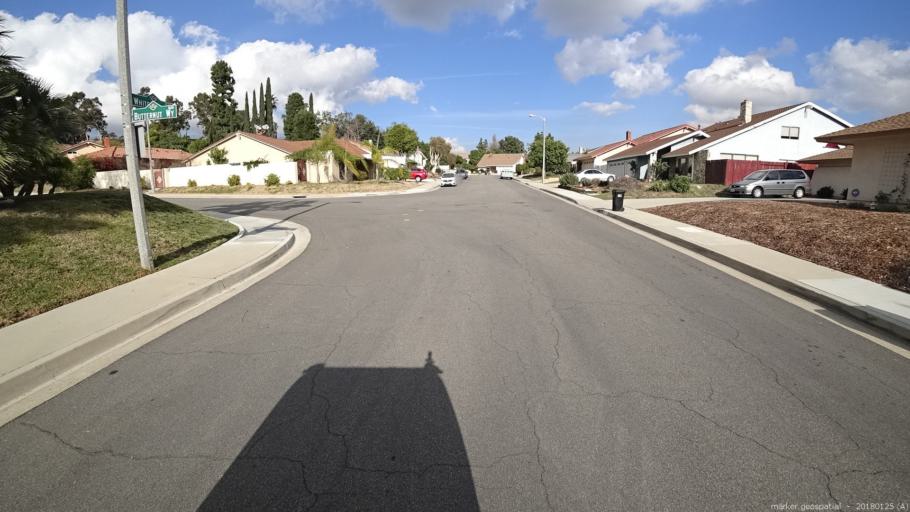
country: US
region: California
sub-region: Los Angeles County
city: Diamond Bar
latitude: 33.9918
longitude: -117.8194
